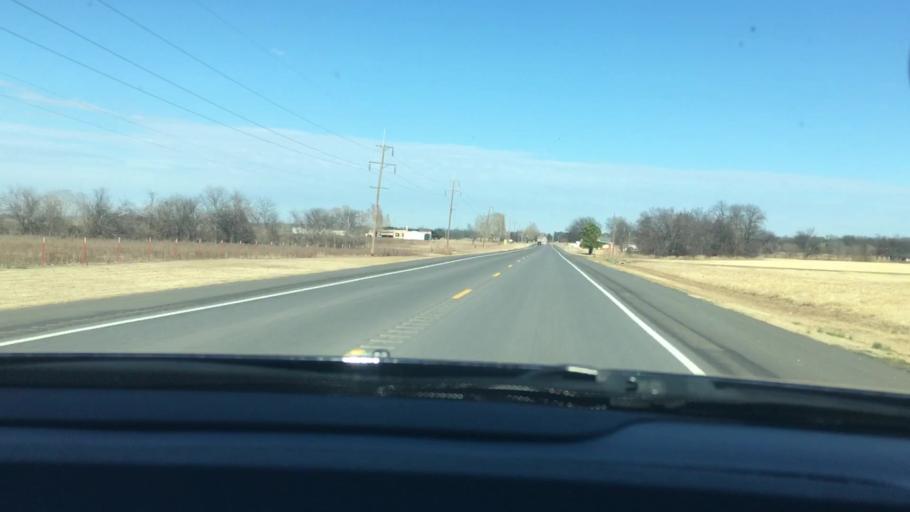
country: US
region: Oklahoma
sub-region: Garvin County
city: Wynnewood
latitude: 34.5883
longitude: -97.1425
